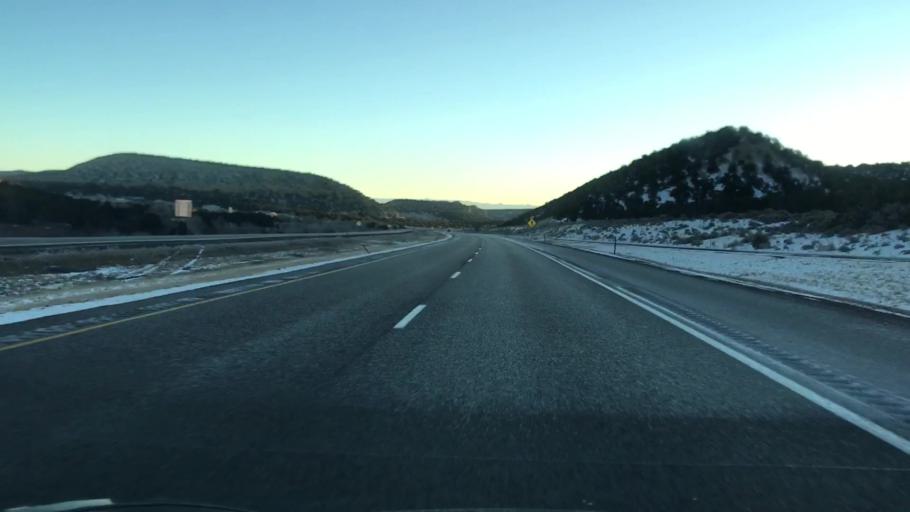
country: US
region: Utah
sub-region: Wayne County
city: Loa
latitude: 38.7576
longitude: -111.4208
